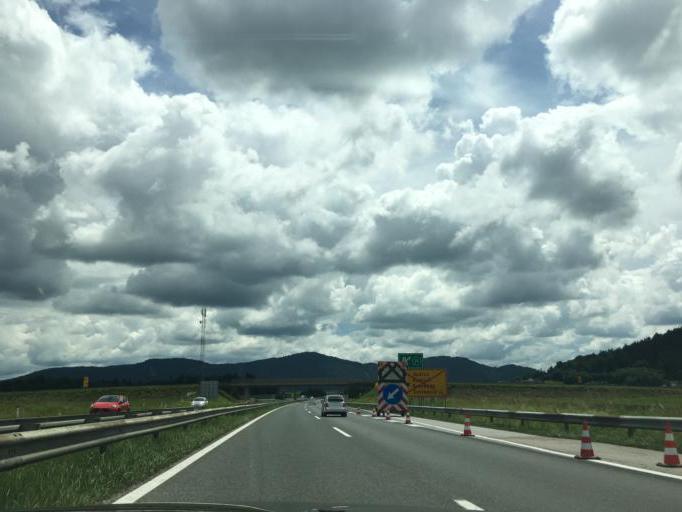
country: SI
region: Vodice
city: Vodice
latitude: 46.1862
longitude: 14.4816
